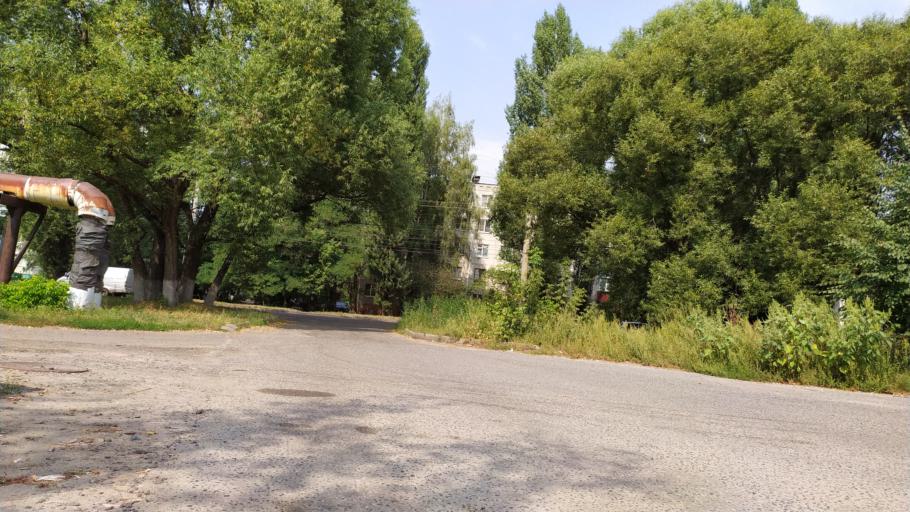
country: RU
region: Kursk
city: Kursk
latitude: 51.6491
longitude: 36.1376
